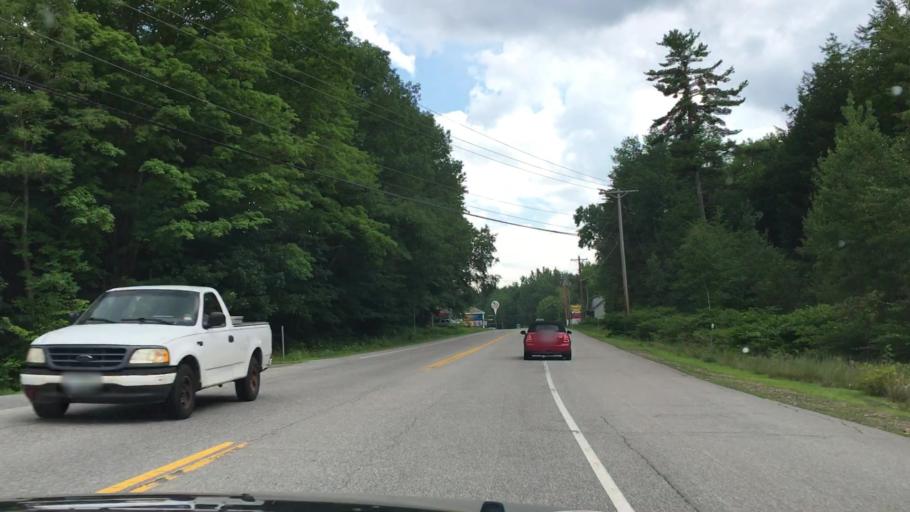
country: US
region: New Hampshire
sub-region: Belknap County
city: Meredith
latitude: 43.6307
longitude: -71.4868
